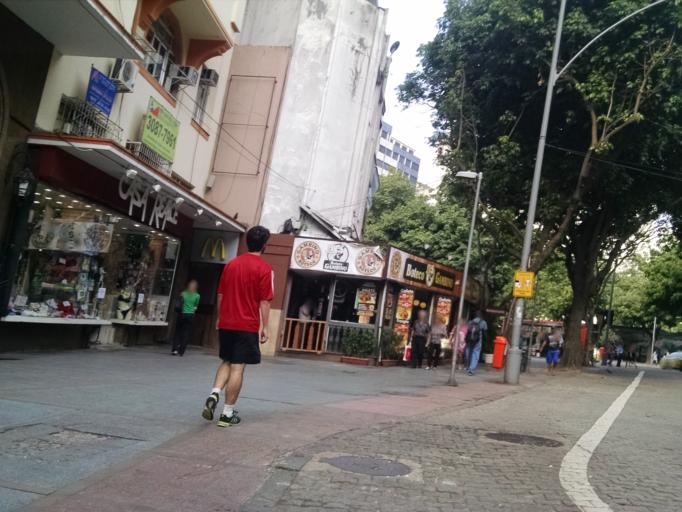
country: BR
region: Rio de Janeiro
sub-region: Rio De Janeiro
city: Rio de Janeiro
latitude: -22.9303
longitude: -43.1783
